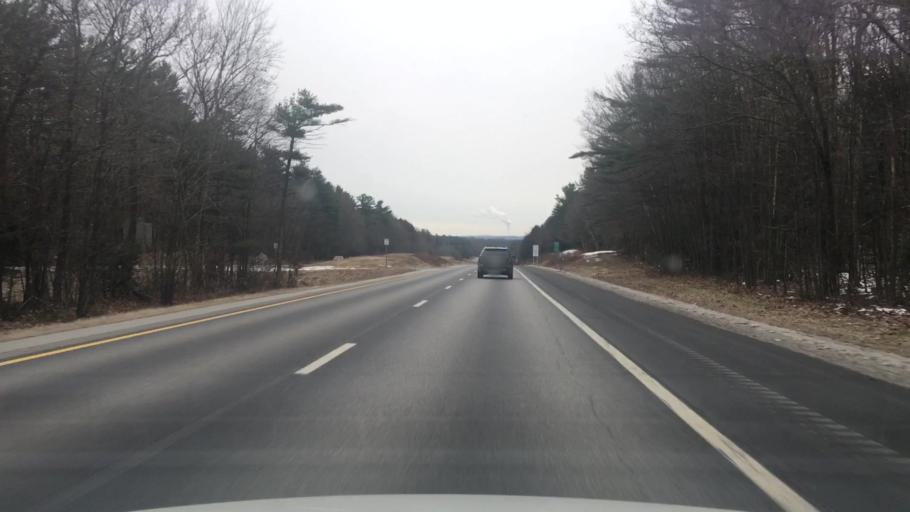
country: US
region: New Hampshire
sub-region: Merrimack County
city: Hopkinton
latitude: 43.1820
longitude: -71.6441
